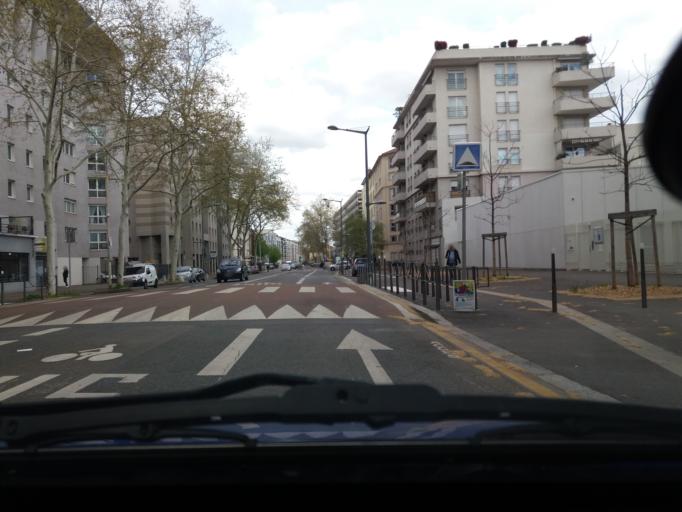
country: FR
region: Rhone-Alpes
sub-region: Departement du Rhone
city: Lyon
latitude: 45.7365
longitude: 4.8647
